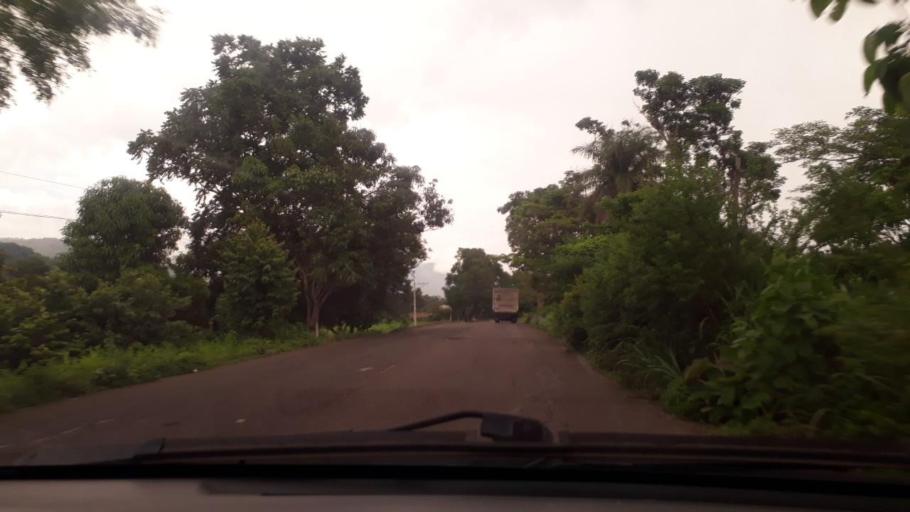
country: GT
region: Jutiapa
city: Jalpatagua
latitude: 14.1497
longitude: -90.0377
